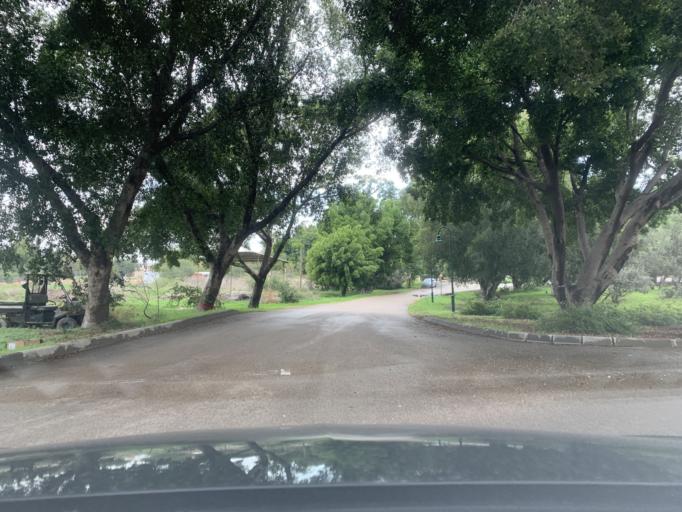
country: PS
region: West Bank
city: Qalqilyah
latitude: 32.2101
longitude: 34.9776
